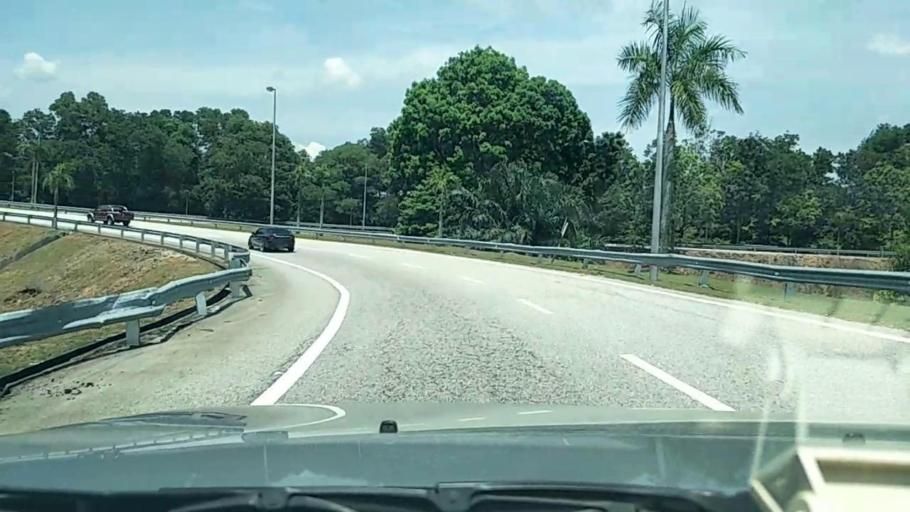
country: MY
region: Putrajaya
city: Putrajaya
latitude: 2.9267
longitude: 101.6662
